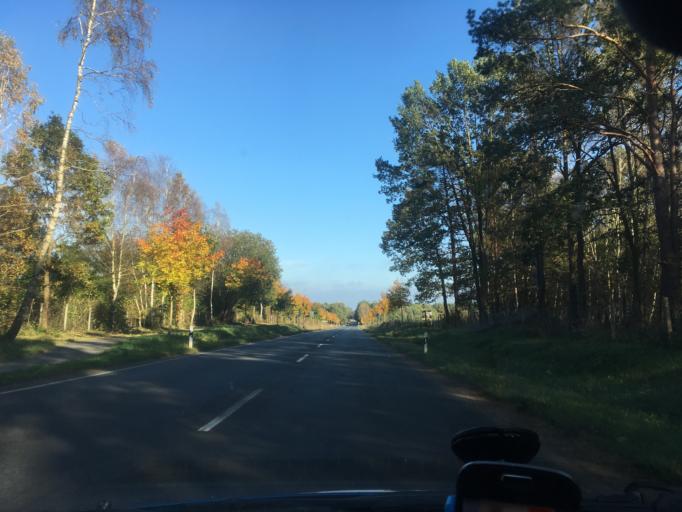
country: DE
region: Lower Saxony
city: Wietzendorf
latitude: 52.9325
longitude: 9.9721
